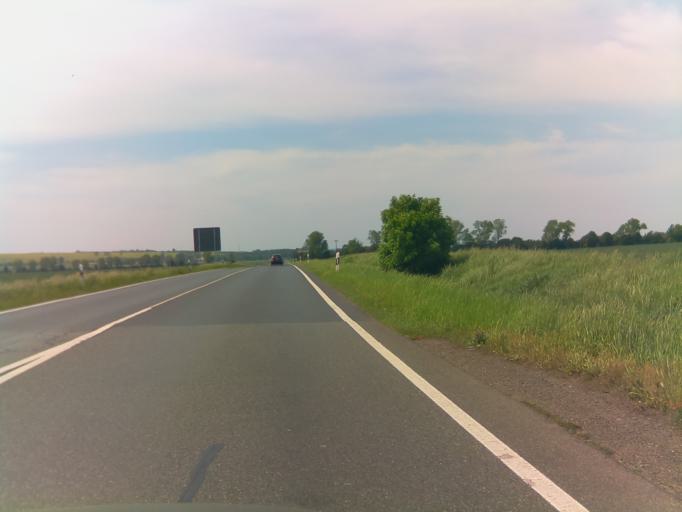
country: DE
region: Saxony-Anhalt
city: Westeregeln
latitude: 51.9406
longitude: 11.3721
